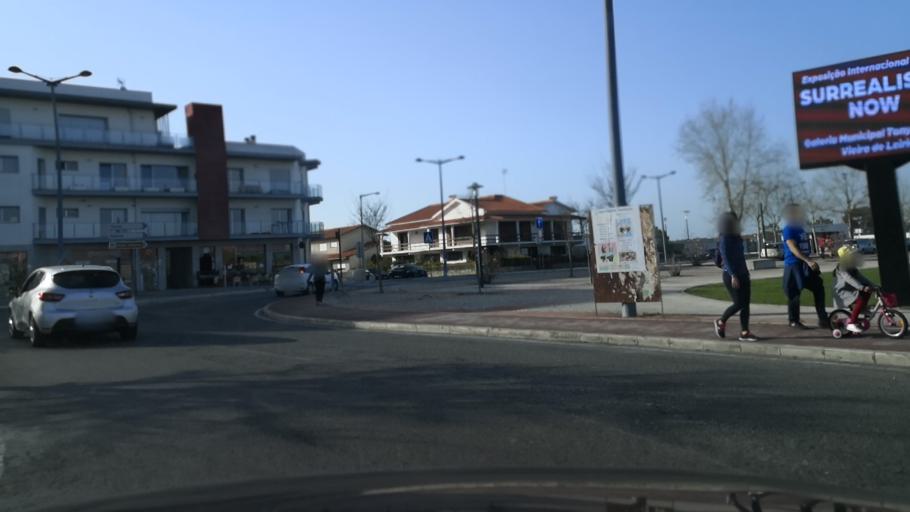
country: PT
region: Leiria
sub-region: Marinha Grande
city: Marinha Grande
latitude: 39.7477
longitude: -8.9363
